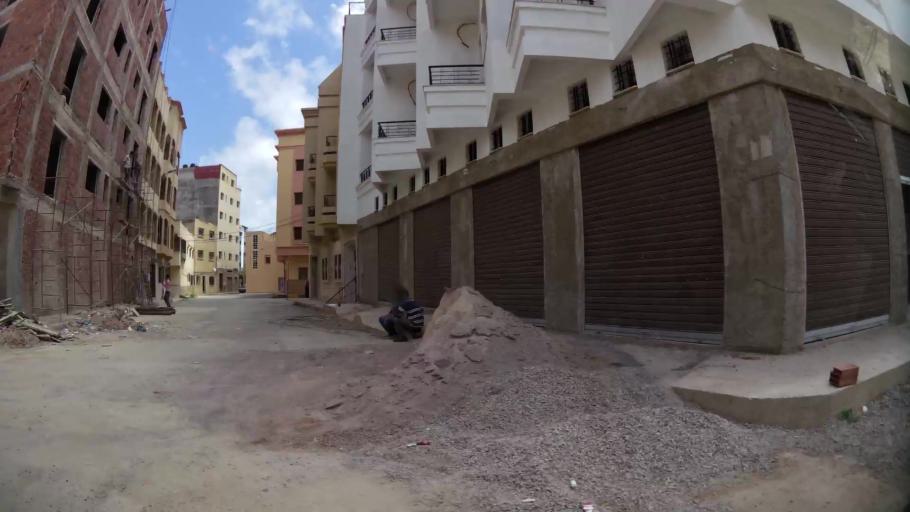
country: MA
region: Oriental
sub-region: Nador
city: Nador
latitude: 35.1683
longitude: -2.9202
